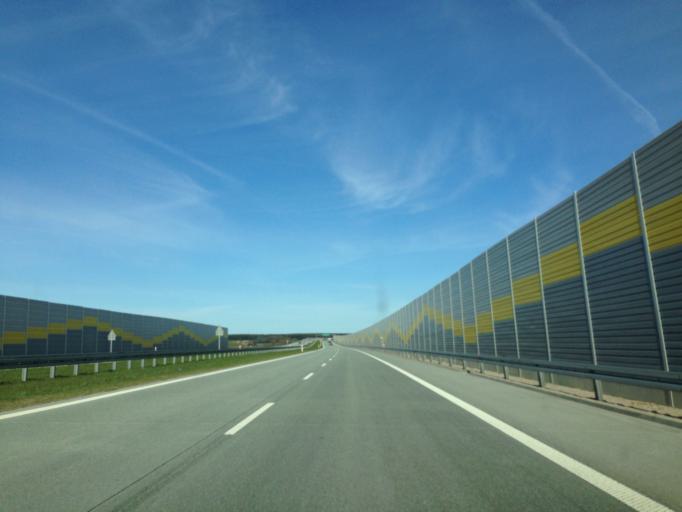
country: PL
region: Lodz Voivodeship
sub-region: Powiat sieradzki
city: Sieradz
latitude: 51.5759
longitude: 18.7928
